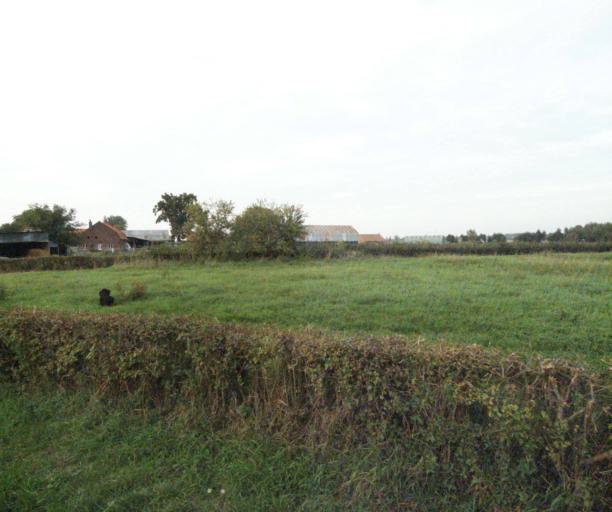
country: FR
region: Nord-Pas-de-Calais
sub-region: Departement du Nord
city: Attiches
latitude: 50.5333
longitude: 3.0555
